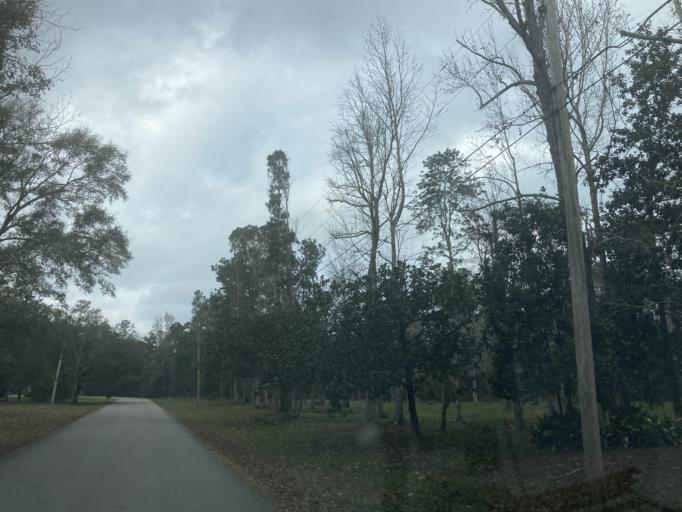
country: US
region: Mississippi
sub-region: Harrison County
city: West Gulfport
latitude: 30.4746
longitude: -89.0084
